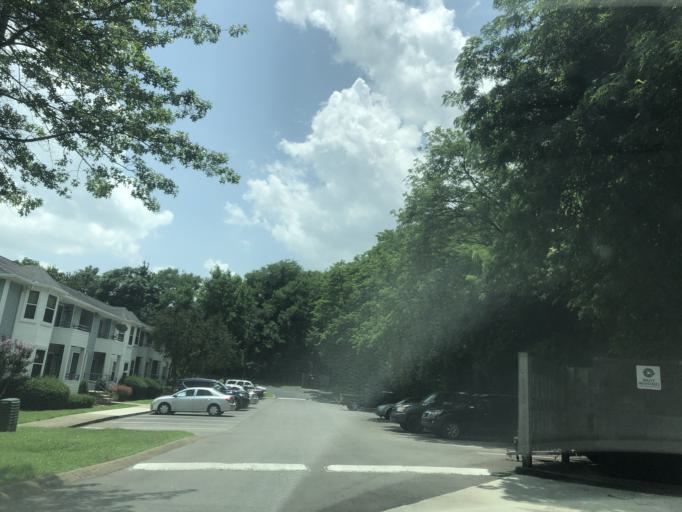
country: US
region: Tennessee
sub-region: Williamson County
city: Nolensville
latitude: 36.0500
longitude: -86.6771
